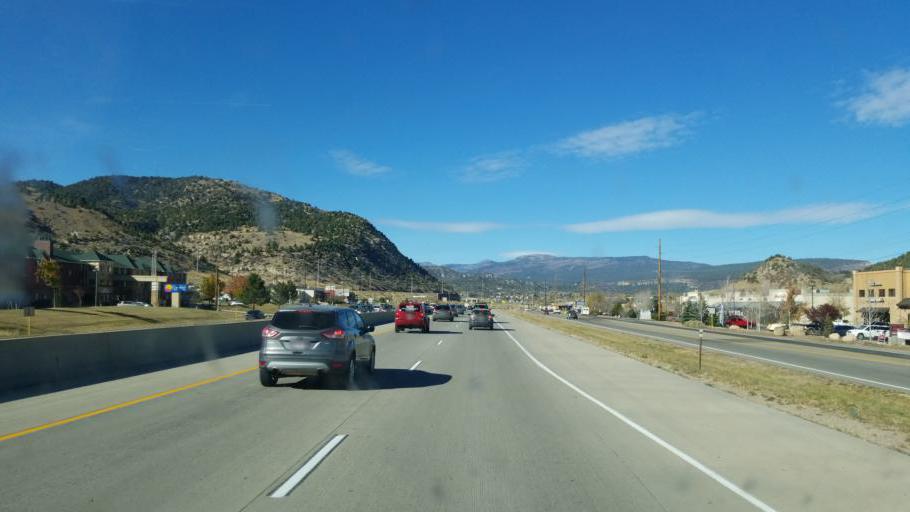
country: US
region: Colorado
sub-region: La Plata County
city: Durango
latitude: 37.2484
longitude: -107.8747
